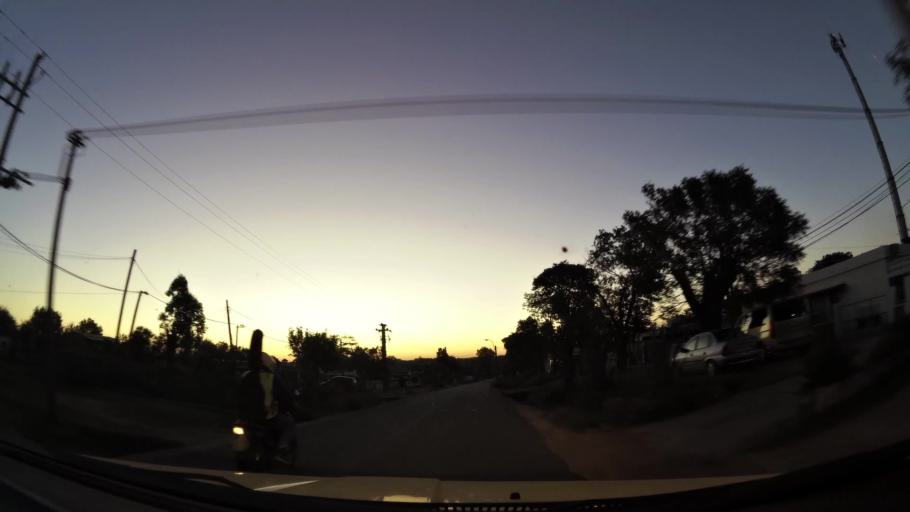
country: UY
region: Canelones
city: La Paz
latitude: -34.8251
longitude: -56.1768
